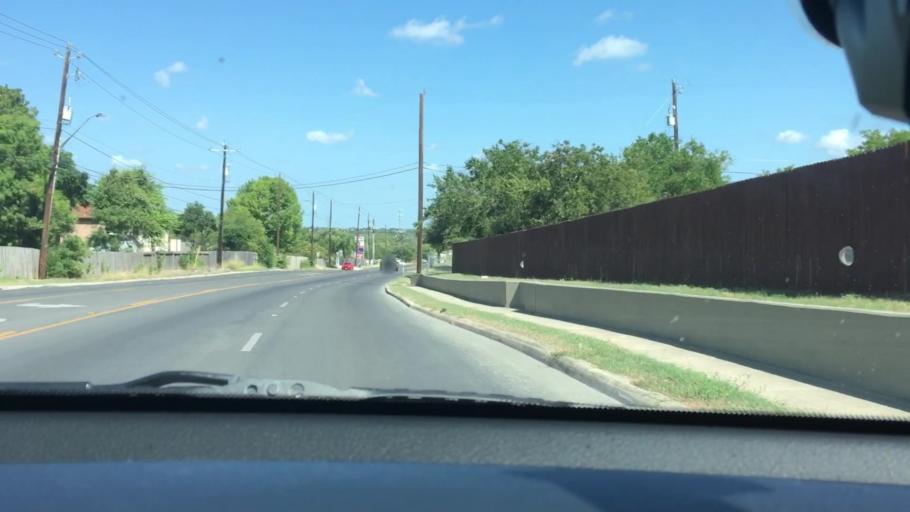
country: US
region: Texas
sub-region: Bexar County
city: Windcrest
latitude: 29.5713
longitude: -98.3964
